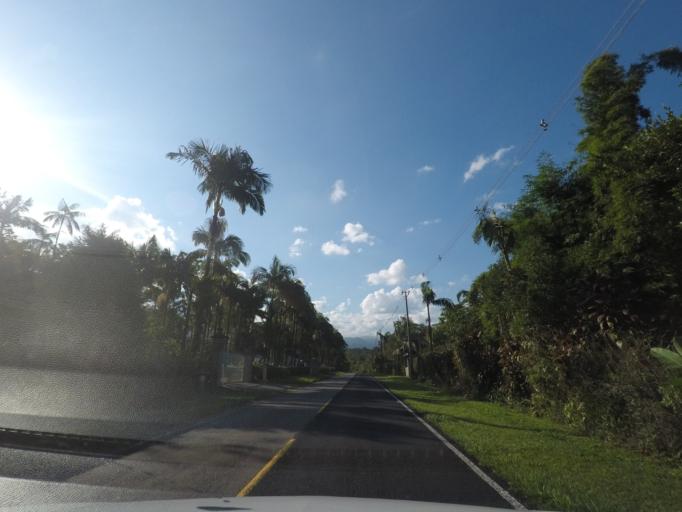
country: BR
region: Parana
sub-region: Antonina
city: Antonina
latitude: -25.4126
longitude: -48.8735
